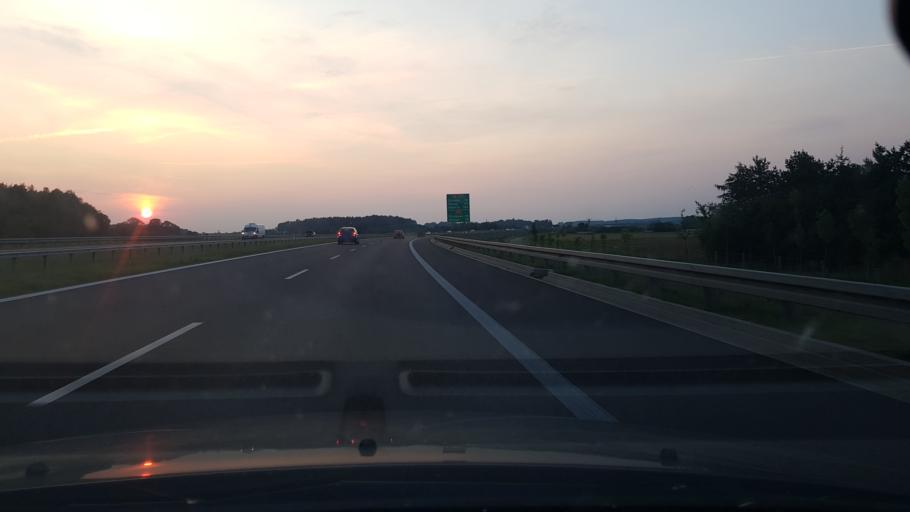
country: PL
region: Warmian-Masurian Voivodeship
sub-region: Powiat nidzicki
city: Nidzica
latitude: 53.3760
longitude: 20.3786
